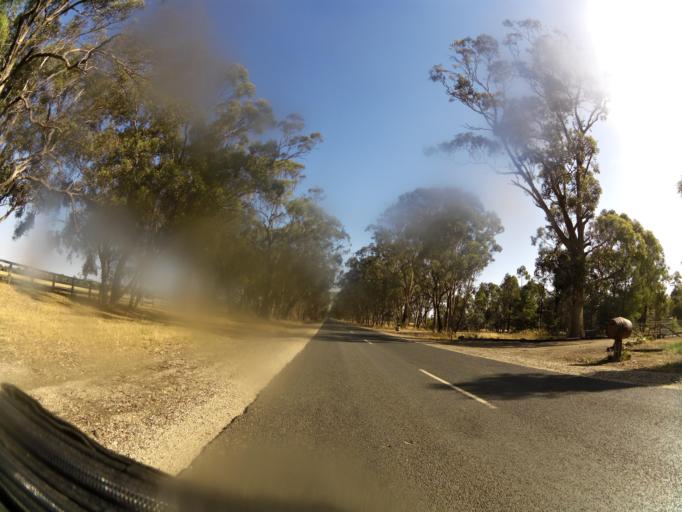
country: AU
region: Victoria
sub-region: Murrindindi
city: Kinglake West
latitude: -36.9652
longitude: 145.1085
